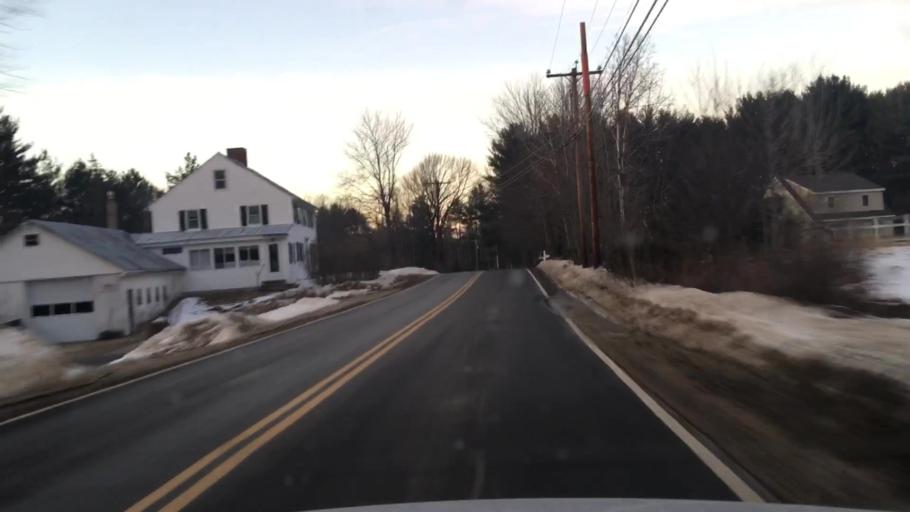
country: US
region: Maine
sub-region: York County
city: Lebanon
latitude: 43.4306
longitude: -70.8817
